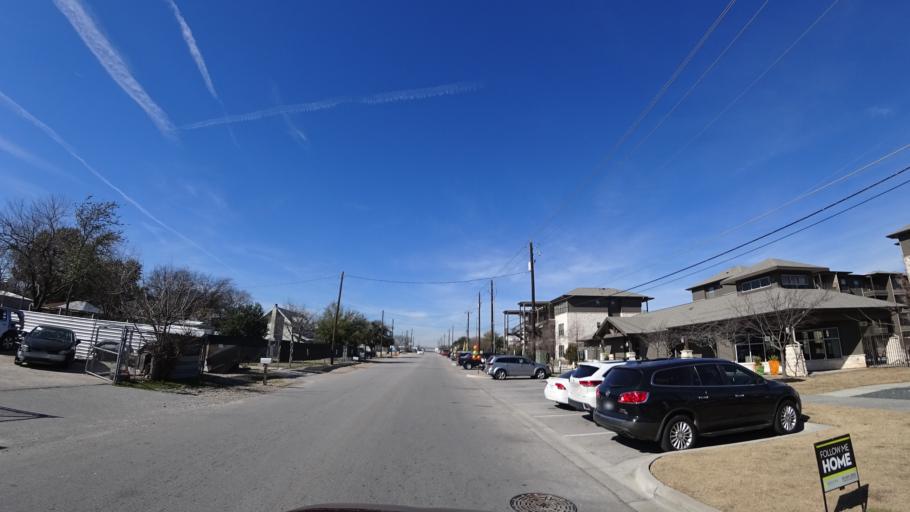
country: US
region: Texas
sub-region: Travis County
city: Wells Branch
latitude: 30.3761
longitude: -97.6854
